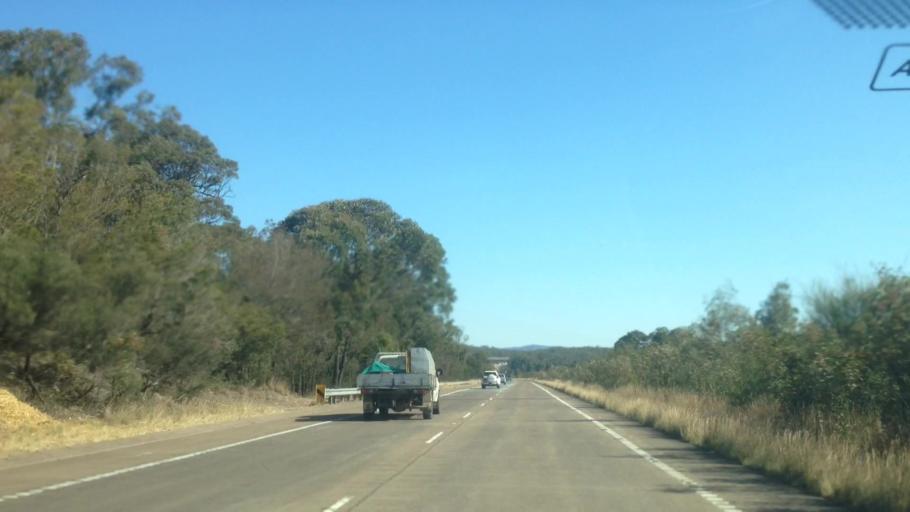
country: AU
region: New South Wales
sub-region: Wyong Shire
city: Jilliby
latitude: -33.2047
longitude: 151.4585
